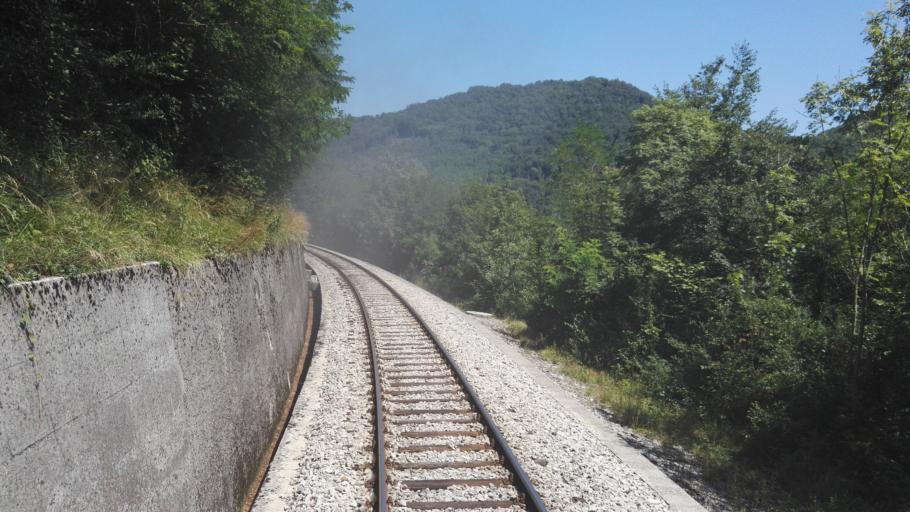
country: SI
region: Kanal
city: Deskle
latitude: 46.0334
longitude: 13.5964
